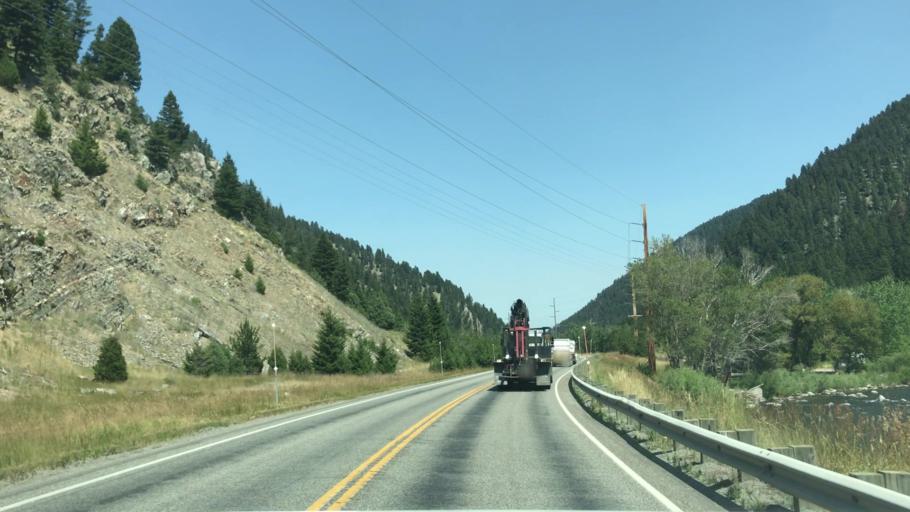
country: US
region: Montana
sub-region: Gallatin County
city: Four Corners
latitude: 45.5011
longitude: -111.2700
